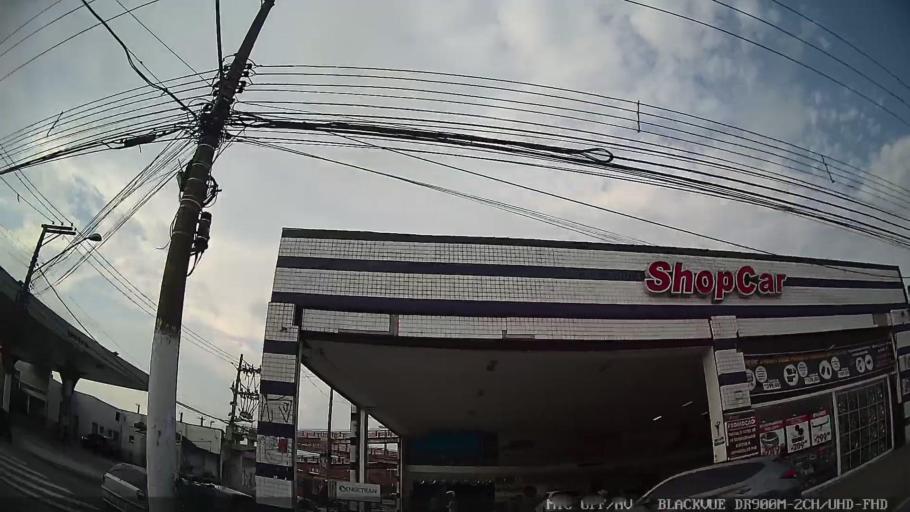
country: BR
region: Sao Paulo
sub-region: Itaquaquecetuba
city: Itaquaquecetuba
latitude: -23.4948
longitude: -46.4064
